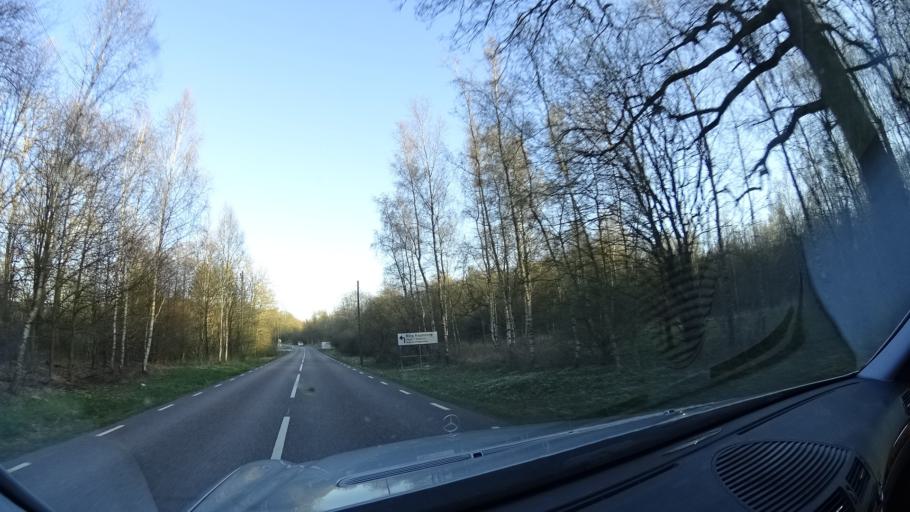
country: SE
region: Skane
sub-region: Svalovs Kommun
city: Kagerod
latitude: 55.9903
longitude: 13.1016
